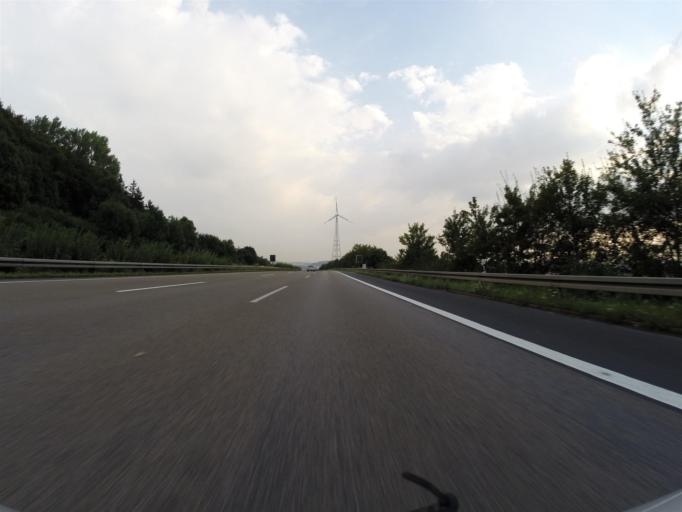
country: DE
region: Hesse
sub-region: Regierungsbezirk Kassel
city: Malsfeld
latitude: 51.0992
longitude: 9.4843
